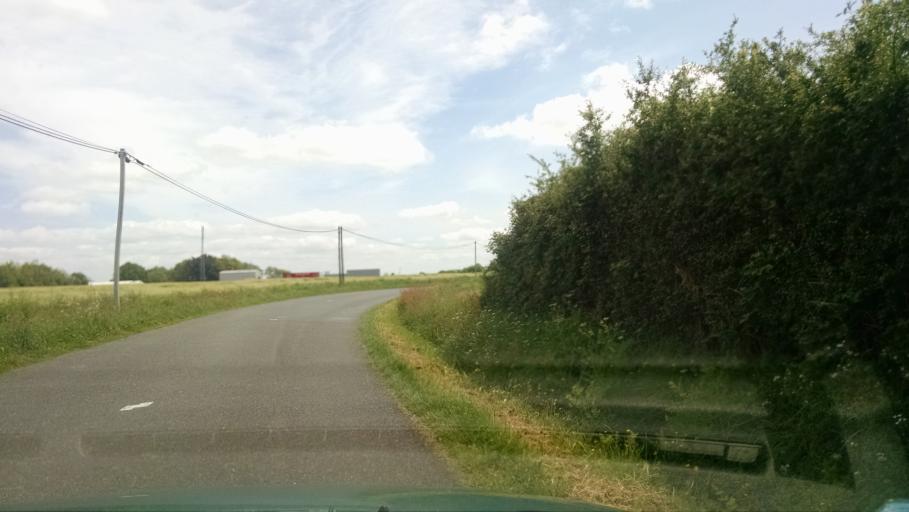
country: FR
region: Pays de la Loire
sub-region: Departement de la Loire-Atlantique
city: Saint-Hilaire-de-Clisson
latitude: 47.0699
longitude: -1.3092
